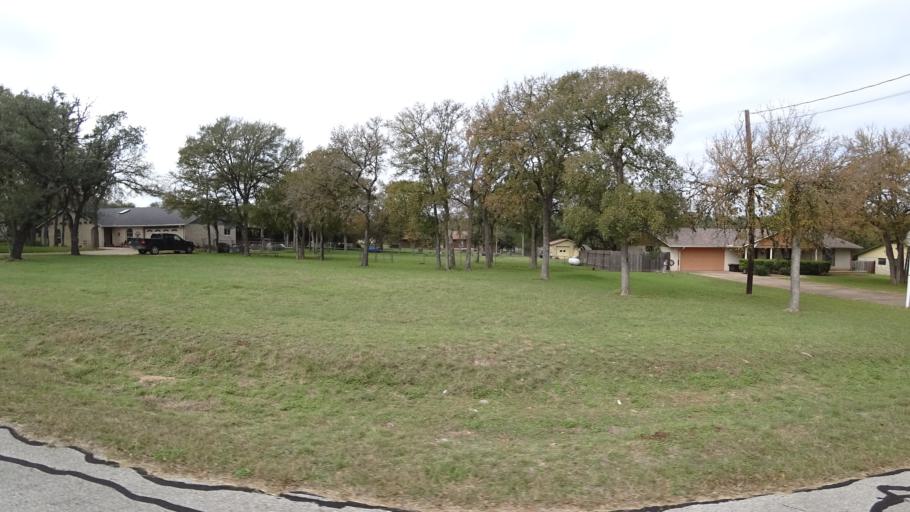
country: US
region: Texas
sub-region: Travis County
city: Shady Hollow
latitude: 30.1374
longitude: -97.8872
